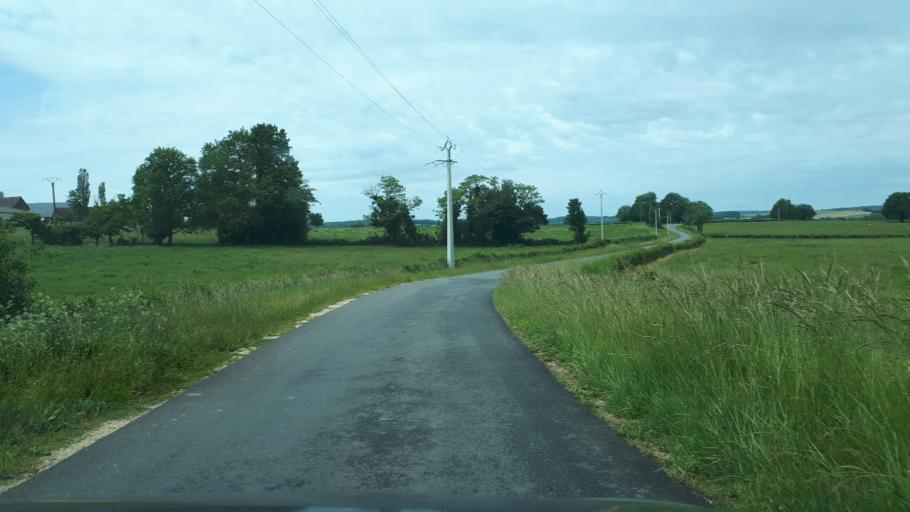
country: FR
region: Centre
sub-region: Departement du Cher
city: Savigny-en-Sancerre
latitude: 47.3950
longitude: 2.6709
